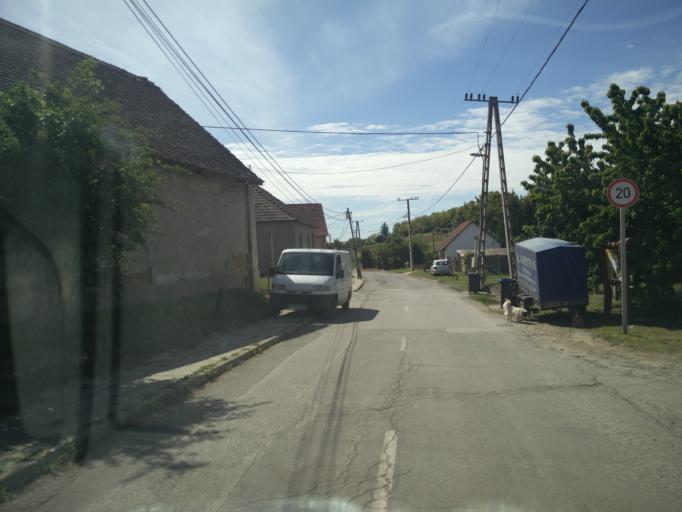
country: HU
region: Tolna
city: Szekszard
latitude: 46.3107
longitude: 18.6843
